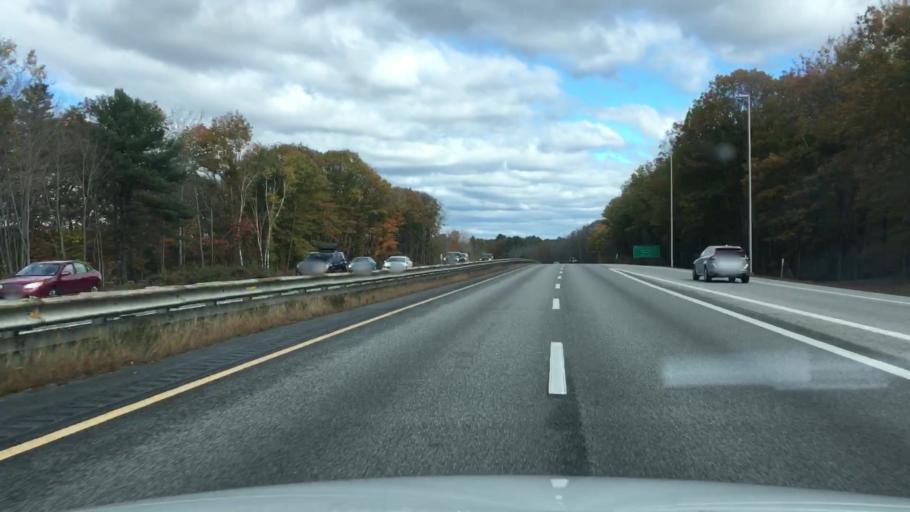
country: US
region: Maine
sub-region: Cumberland County
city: Freeport
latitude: 43.8471
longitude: -70.1183
